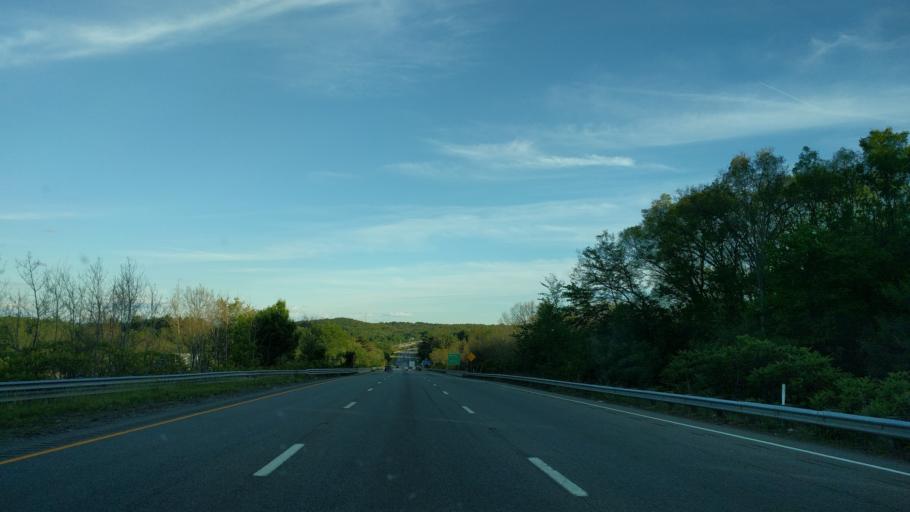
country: US
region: Massachusetts
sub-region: Middlesex County
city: Marlborough
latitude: 42.3162
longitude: -71.5694
